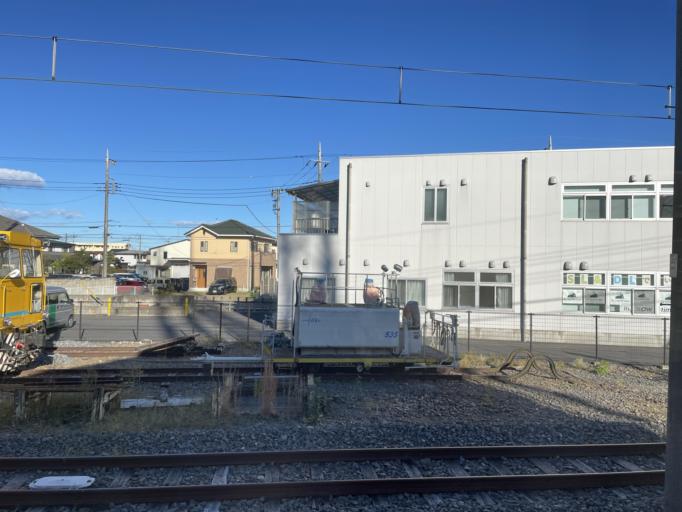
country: JP
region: Tochigi
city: Tochigi
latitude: 36.3897
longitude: 139.7427
